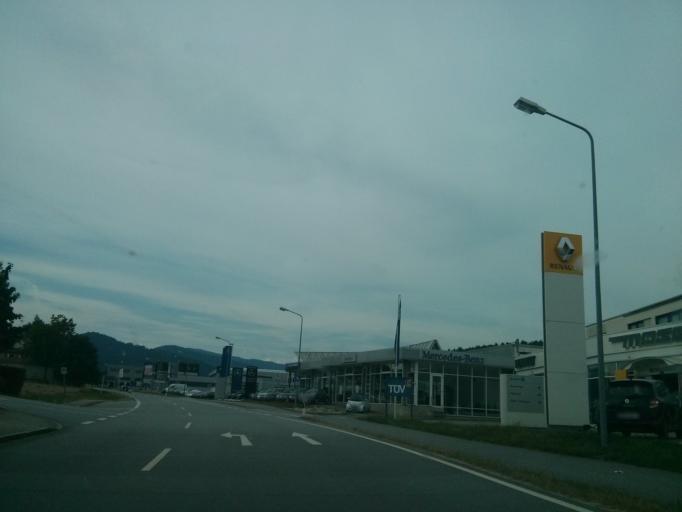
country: DE
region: Bavaria
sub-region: Lower Bavaria
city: Deggendorf
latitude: 48.8549
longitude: 12.9625
